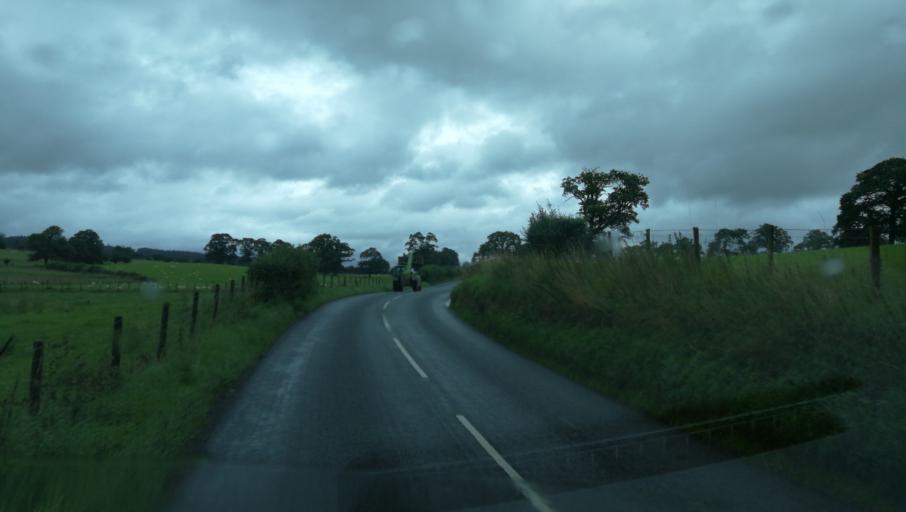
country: GB
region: England
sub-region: Cumbria
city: Penrith
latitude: 54.6167
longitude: -2.8292
